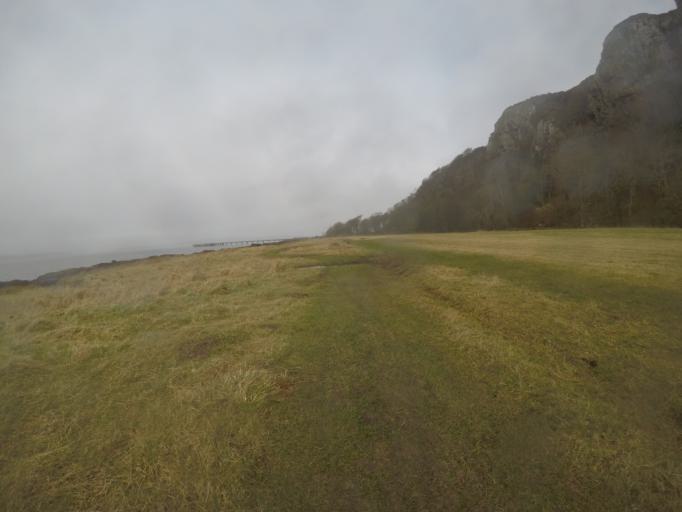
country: GB
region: Scotland
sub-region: North Ayrshire
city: Millport
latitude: 55.7107
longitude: -4.9036
